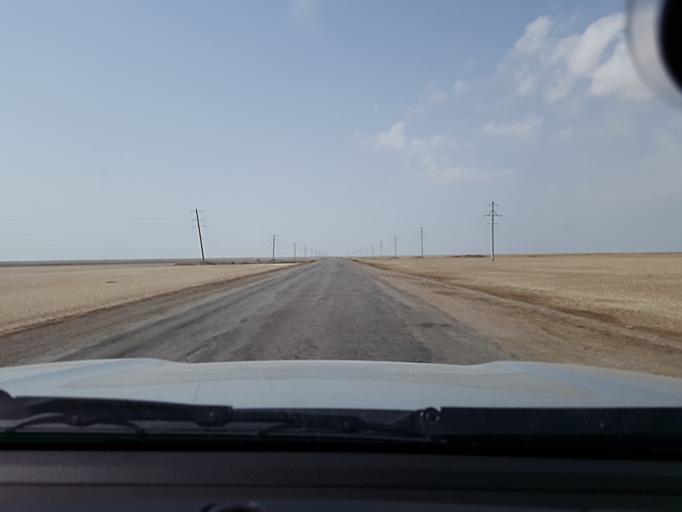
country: TM
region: Balkan
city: Gumdag
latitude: 39.0789
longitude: 54.5842
